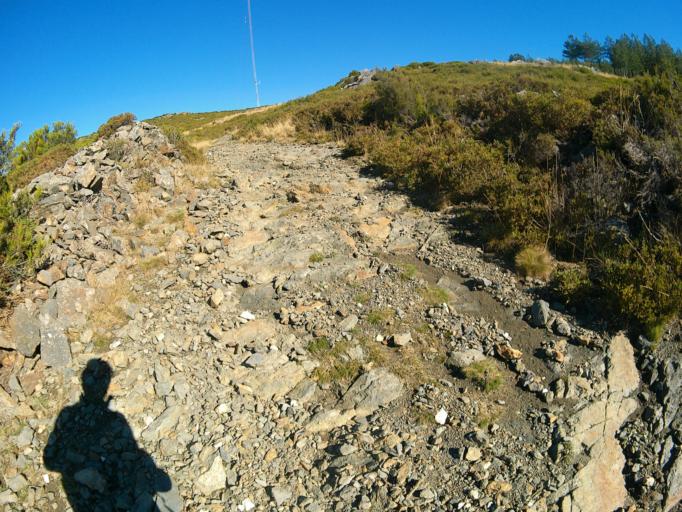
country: PT
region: Vila Real
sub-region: Mesao Frio
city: Mesao Frio
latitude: 41.2428
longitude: -7.9004
